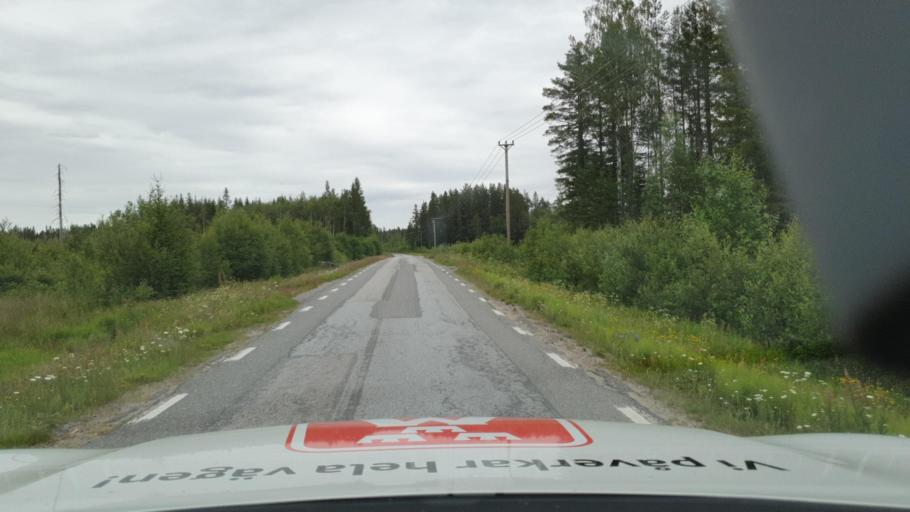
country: SE
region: Vaesterbotten
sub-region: Nordmalings Kommun
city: Nordmaling
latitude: 63.5070
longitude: 19.4189
